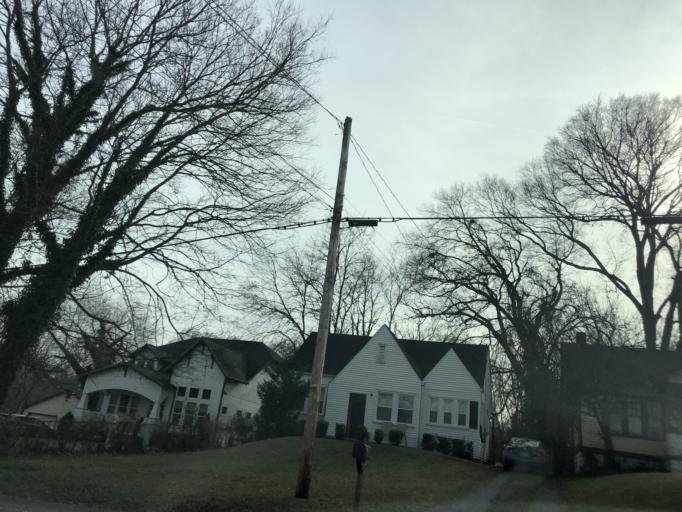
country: US
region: Tennessee
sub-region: Davidson County
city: Nashville
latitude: 36.2083
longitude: -86.7314
